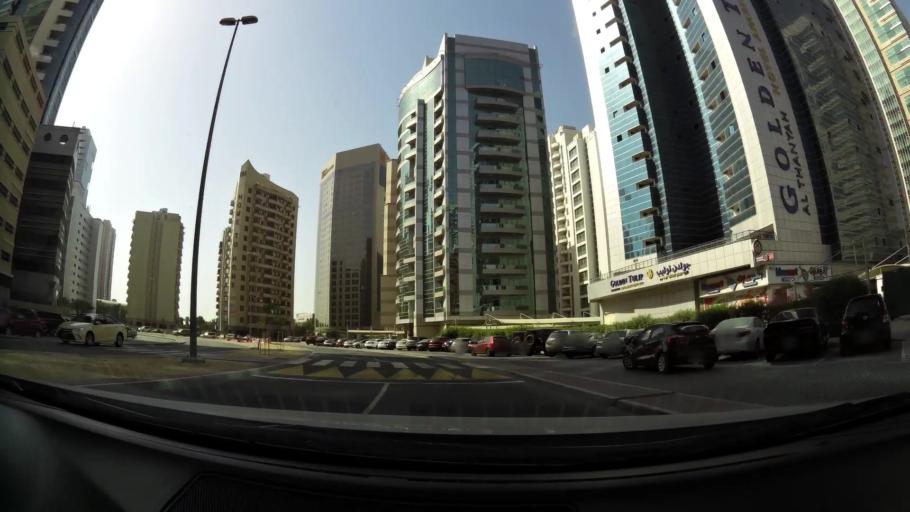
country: AE
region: Dubai
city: Dubai
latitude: 25.0993
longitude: 55.1783
